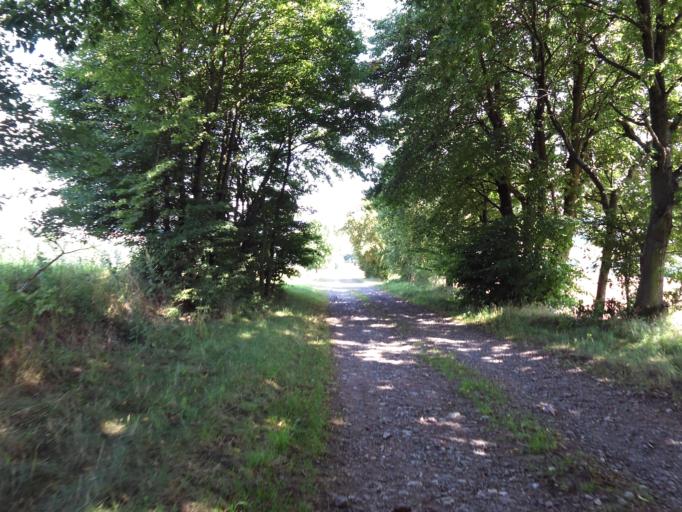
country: DE
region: Rheinland-Pfalz
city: Imsbach
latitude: 49.5822
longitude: 7.9109
